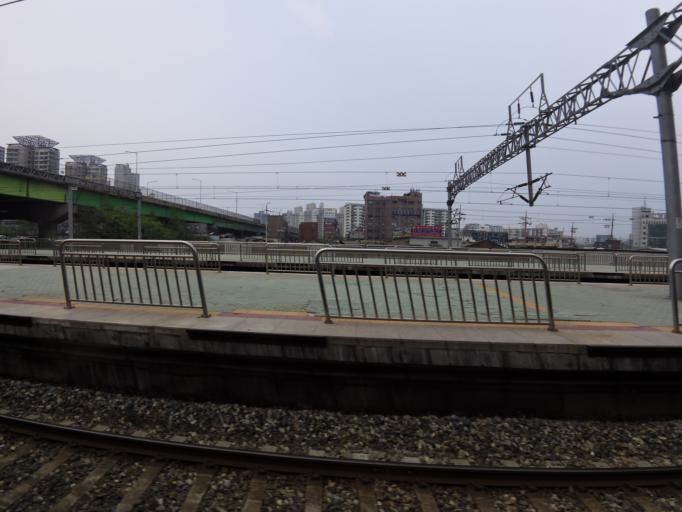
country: KR
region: Gyeonggi-do
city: Kwangmyong
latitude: 37.5100
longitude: 126.8929
